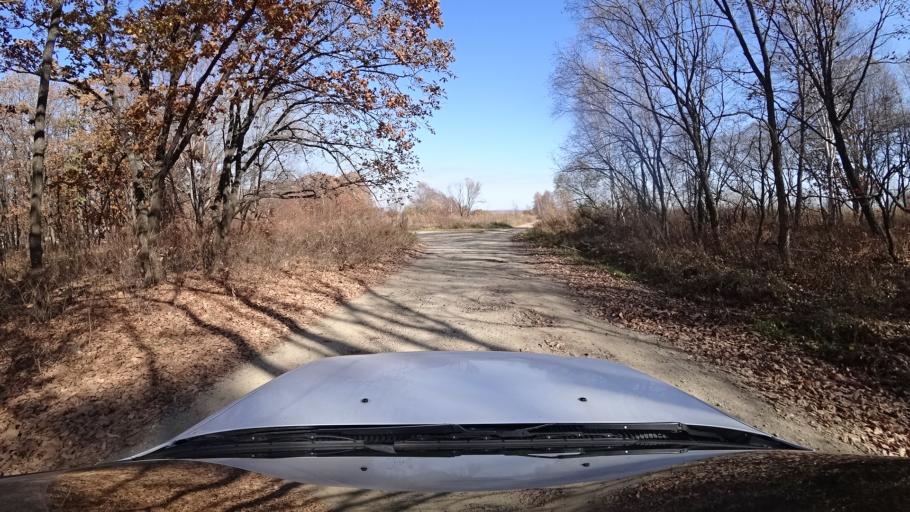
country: RU
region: Primorskiy
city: Dal'nerechensk
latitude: 45.8820
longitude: 133.7345
